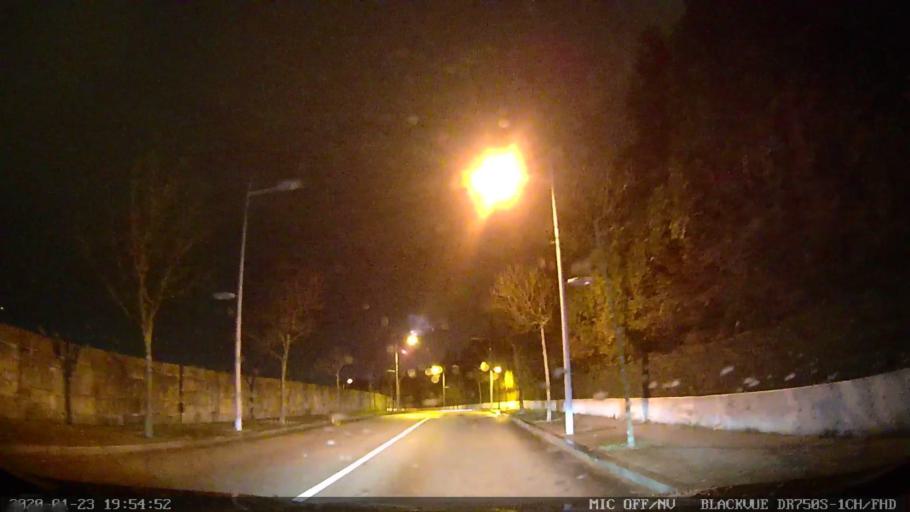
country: PT
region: Porto
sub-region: Matosinhos
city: Santa Cruz do Bispo
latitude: 41.2316
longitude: -8.6574
